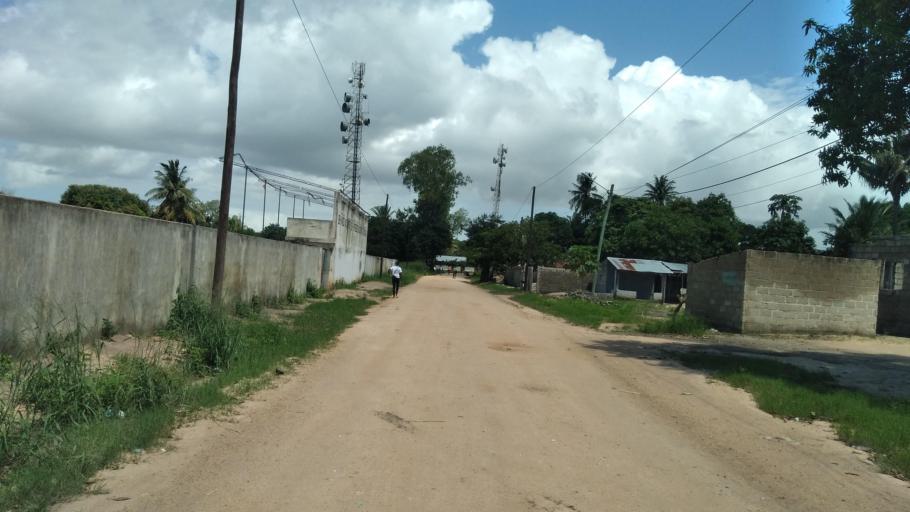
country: MZ
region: Zambezia
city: Quelimane
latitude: -17.5995
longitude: 36.8137
